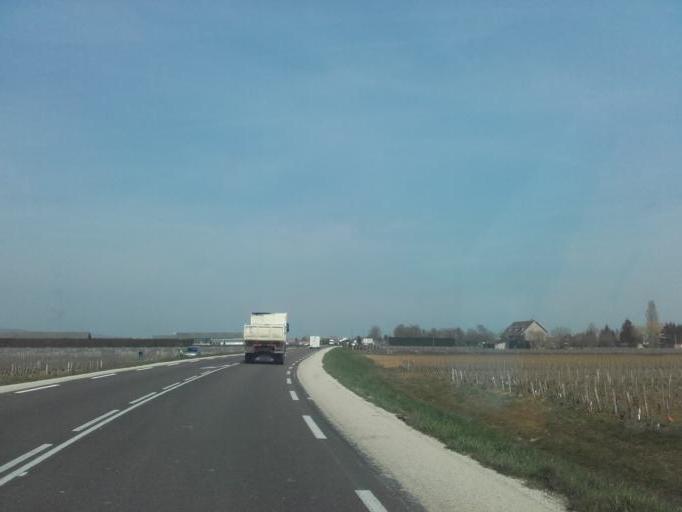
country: FR
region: Bourgogne
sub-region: Departement de la Cote-d'Or
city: Meursault
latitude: 46.9684
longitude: 4.7767
